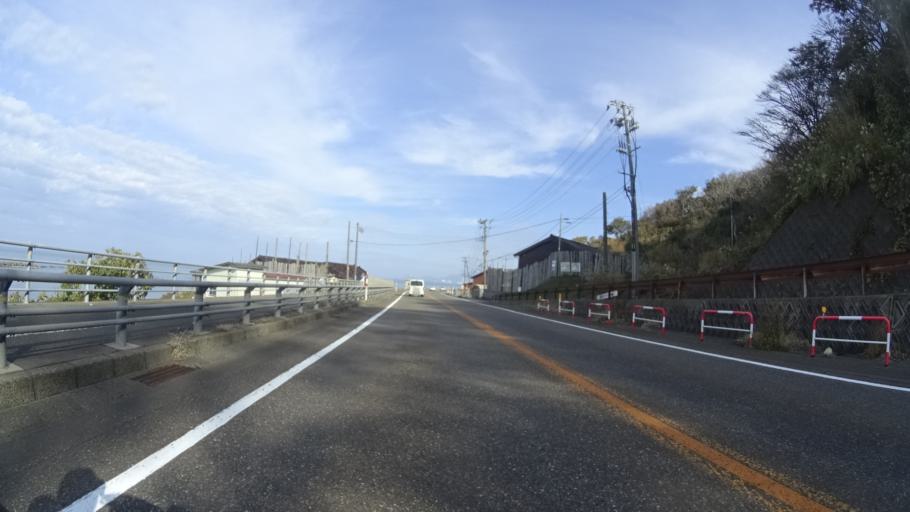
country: JP
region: Niigata
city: Joetsu
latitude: 37.1686
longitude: 138.1927
